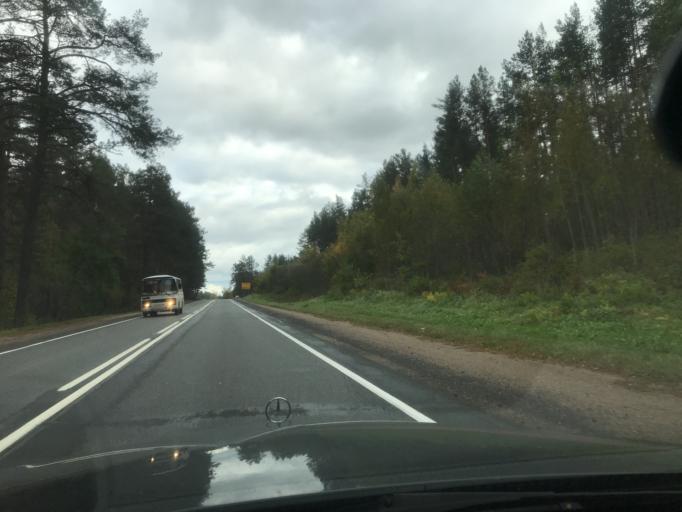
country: RU
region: Pskov
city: Idritsa
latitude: 56.4617
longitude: 29.1051
